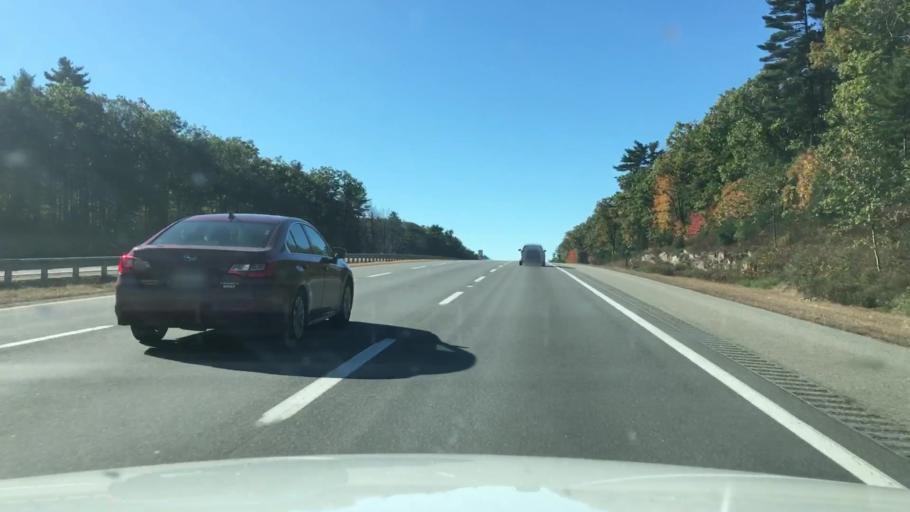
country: US
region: Maine
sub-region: York County
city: West Kennebunk
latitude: 43.3677
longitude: -70.5836
